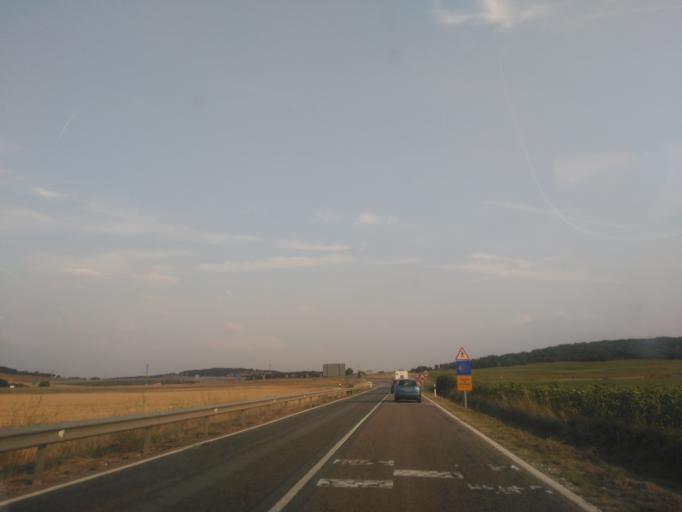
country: ES
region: Castille and Leon
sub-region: Provincia de Zamora
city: Montamarta
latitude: 41.6918
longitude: -5.8108
